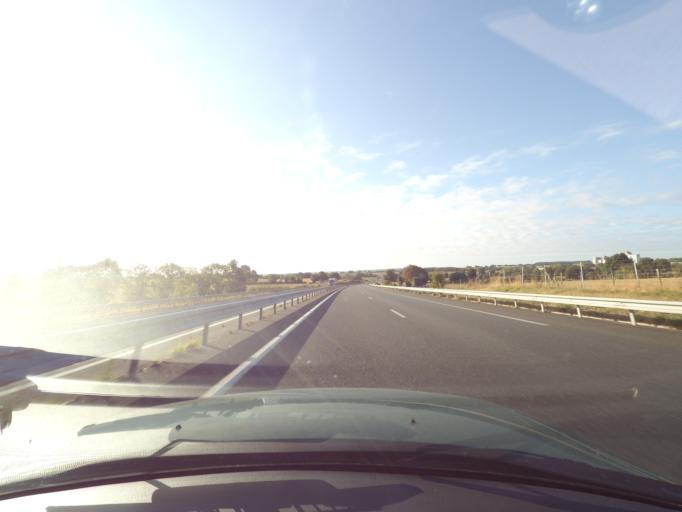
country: FR
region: Poitou-Charentes
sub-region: Departement des Deux-Sevres
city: Combrand
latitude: 46.9151
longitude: -0.6868
